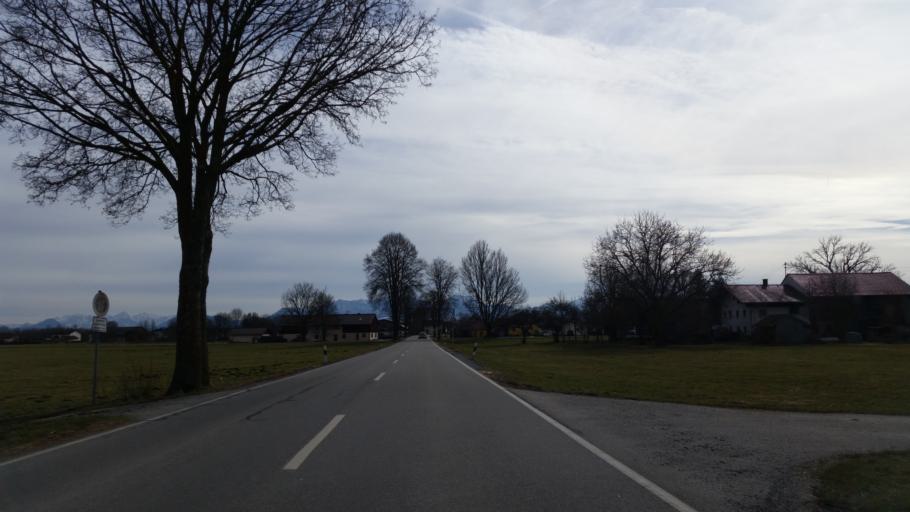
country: DE
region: Bavaria
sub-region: Upper Bavaria
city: Bruckmuhl
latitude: 47.8964
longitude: 11.9258
